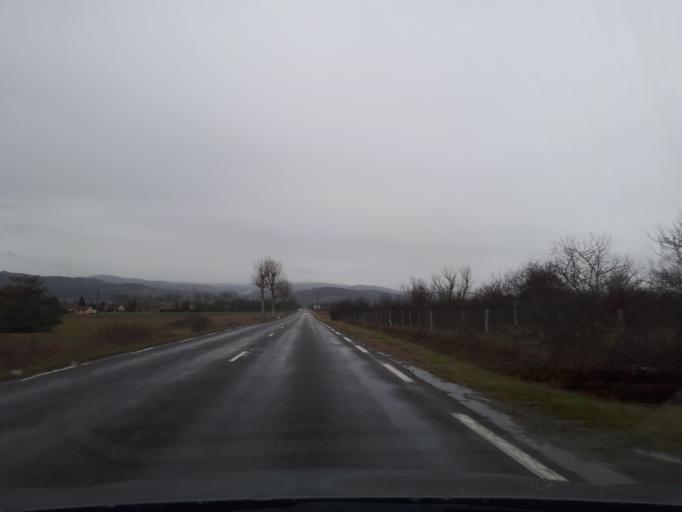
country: FR
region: Rhone-Alpes
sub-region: Departement de la Loire
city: Boen-sur-Lignon
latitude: 45.7385
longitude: 4.0481
